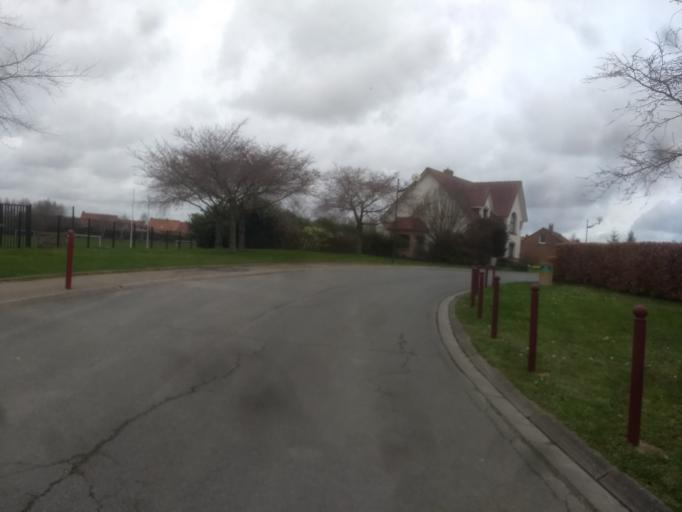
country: FR
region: Nord-Pas-de-Calais
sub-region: Departement du Pas-de-Calais
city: Anzin-Saint-Aubin
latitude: 50.3144
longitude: 2.7557
